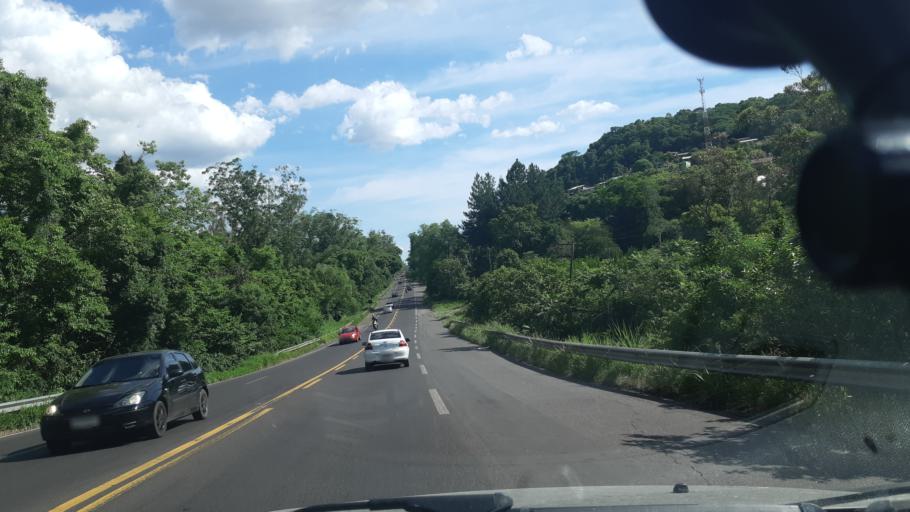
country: BR
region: Rio Grande do Sul
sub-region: Estancia Velha
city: Estancia Velha
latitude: -29.6380
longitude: -51.1420
